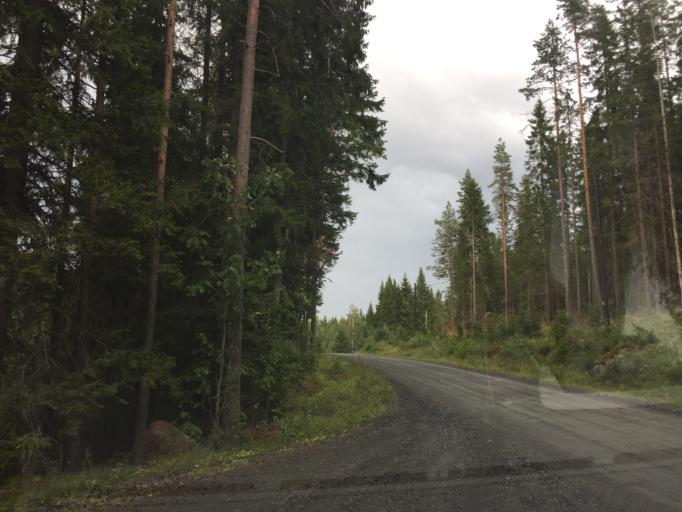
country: SE
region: Vaermland
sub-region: Filipstads Kommun
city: Lesjofors
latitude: 59.9313
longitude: 14.1293
